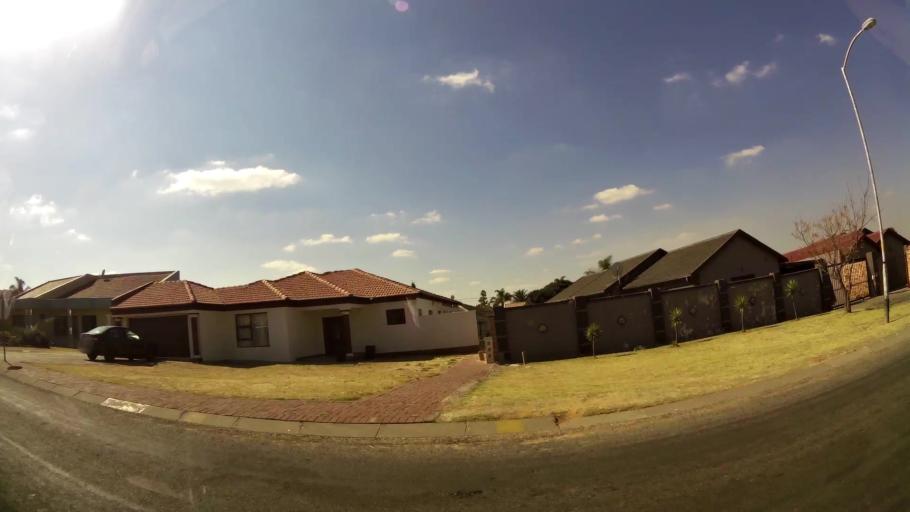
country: ZA
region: Gauteng
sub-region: West Rand District Municipality
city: Randfontein
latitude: -26.1748
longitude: 27.7472
